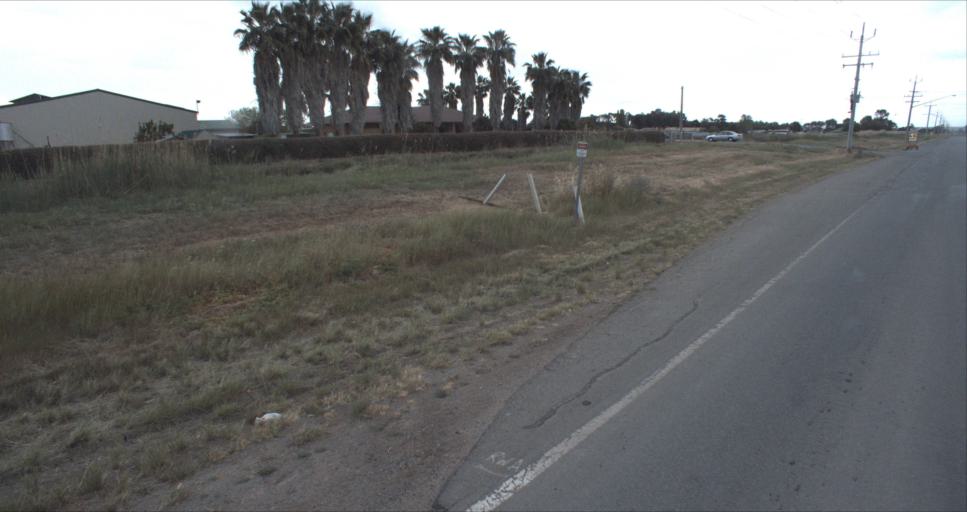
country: AU
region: New South Wales
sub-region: Leeton
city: Leeton
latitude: -34.5469
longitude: 146.3858
